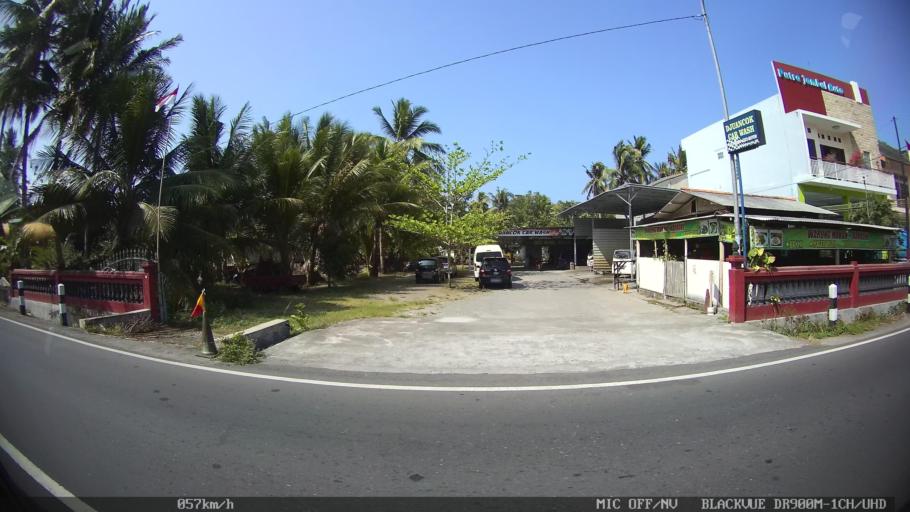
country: ID
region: Daerah Istimewa Yogyakarta
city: Srandakan
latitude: -7.9297
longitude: 110.1994
